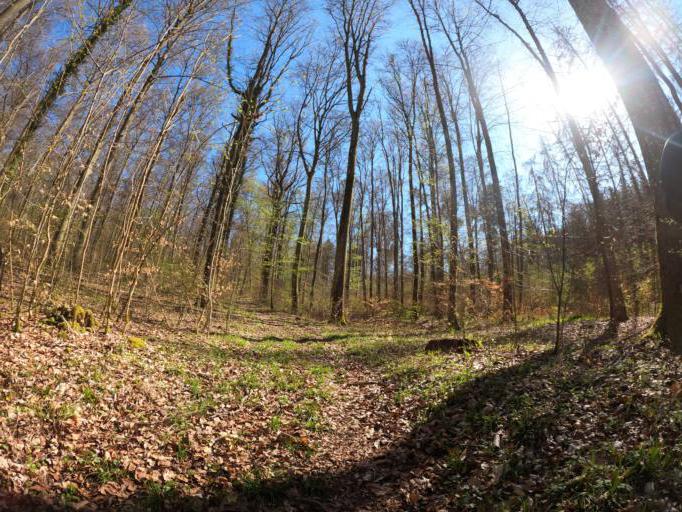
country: DE
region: Baden-Wuerttemberg
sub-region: Karlsruhe Region
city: Monsheim
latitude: 48.9049
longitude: 8.9045
